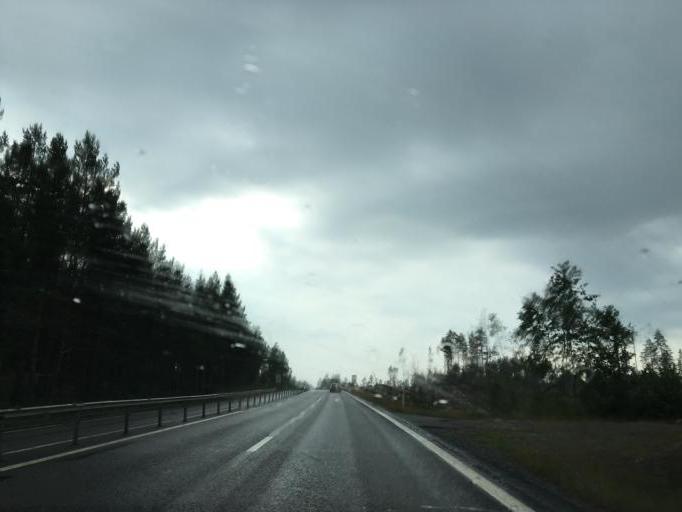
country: SE
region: OEstergoetland
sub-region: Norrkopings Kommun
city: Jursla
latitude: 58.7684
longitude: 16.1674
